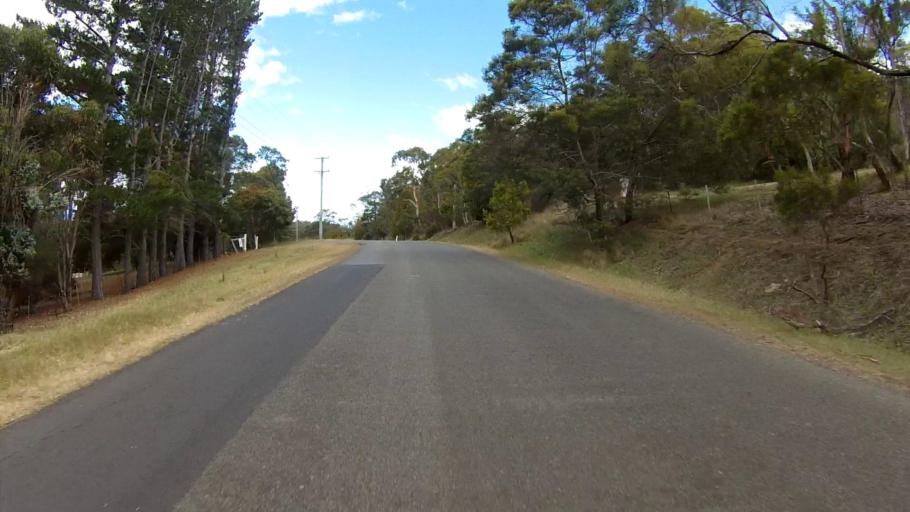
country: AU
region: Tasmania
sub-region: Clarence
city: Acton Park
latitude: -42.8679
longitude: 147.4703
